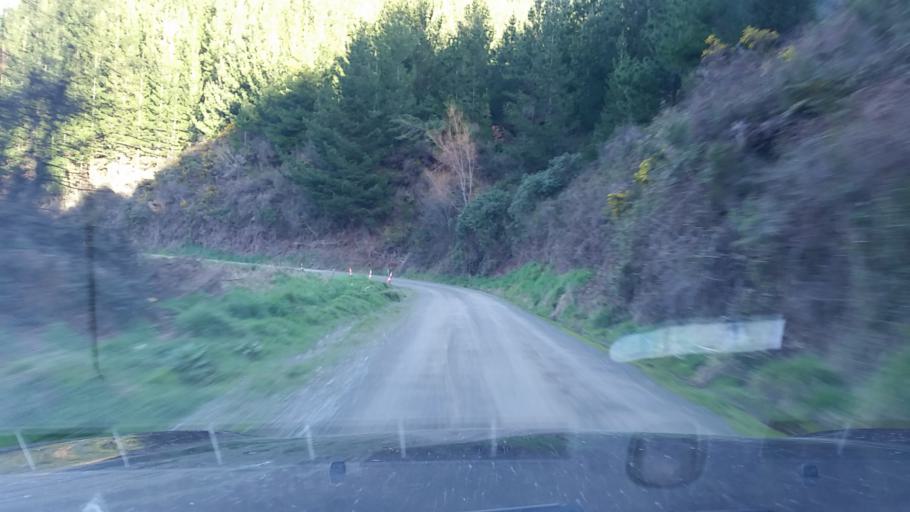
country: NZ
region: Nelson
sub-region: Nelson City
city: Nelson
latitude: -41.5616
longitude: 173.4319
